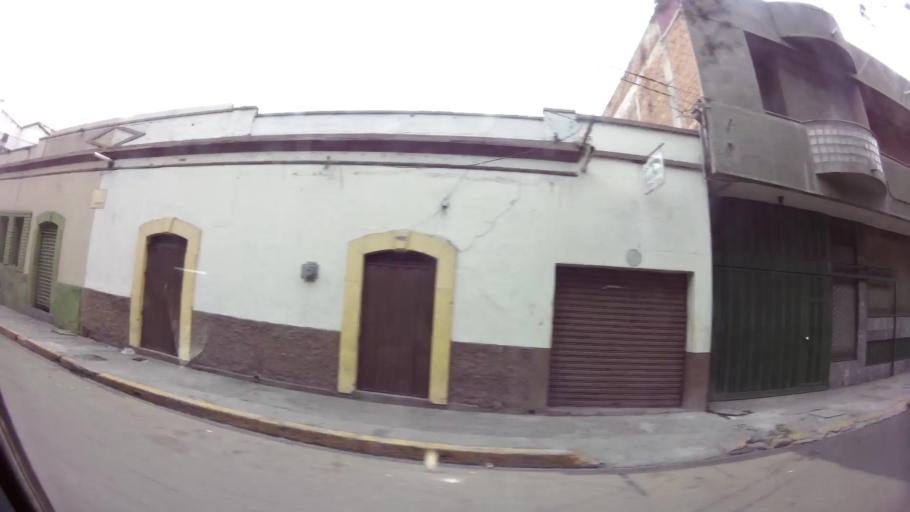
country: HN
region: Francisco Morazan
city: Tegucigalpa
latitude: 14.0933
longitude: -87.2078
